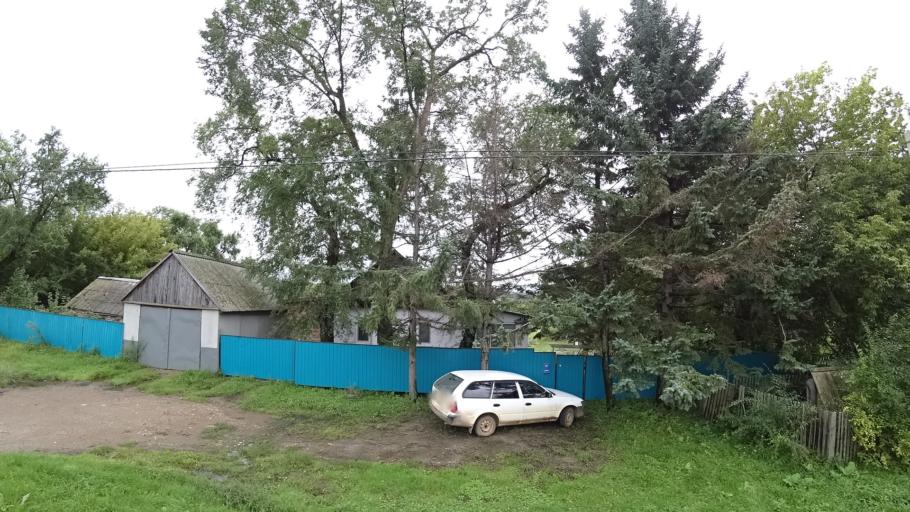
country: RU
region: Primorskiy
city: Monastyrishche
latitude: 44.0796
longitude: 132.5826
